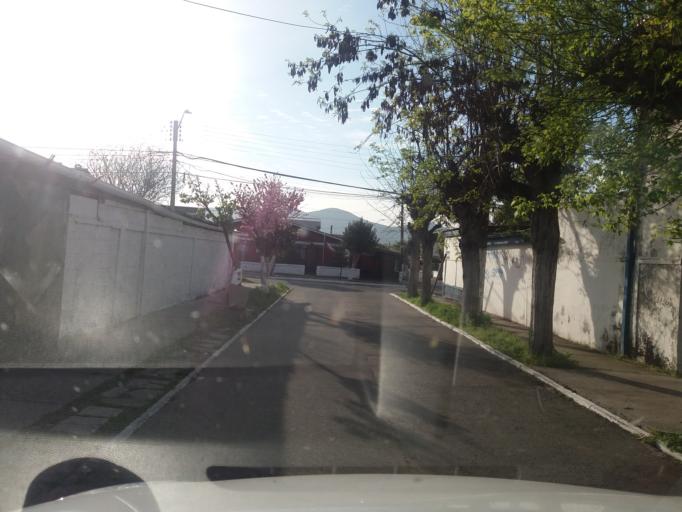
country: CL
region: Valparaiso
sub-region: Provincia de Quillota
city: Hacienda La Calera
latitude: -32.7815
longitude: -71.1781
